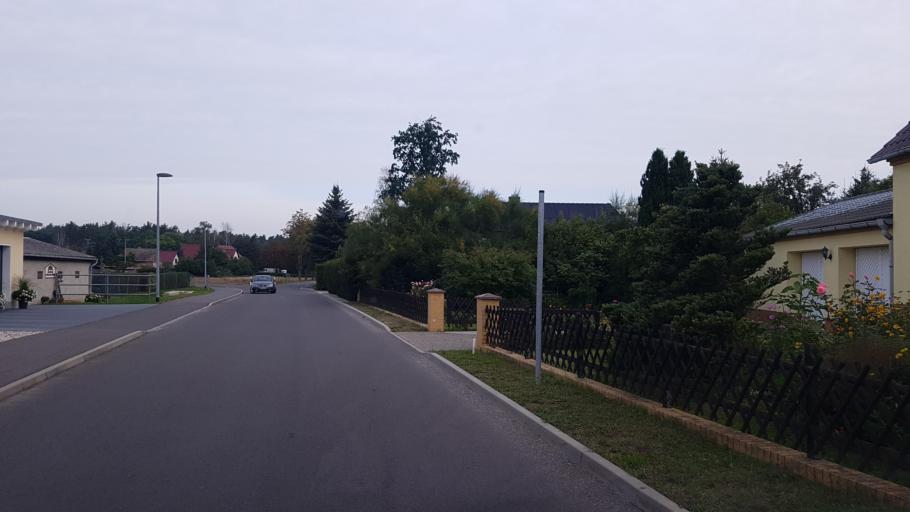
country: DE
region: Brandenburg
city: Sonnewalde
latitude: 51.7774
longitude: 13.6216
